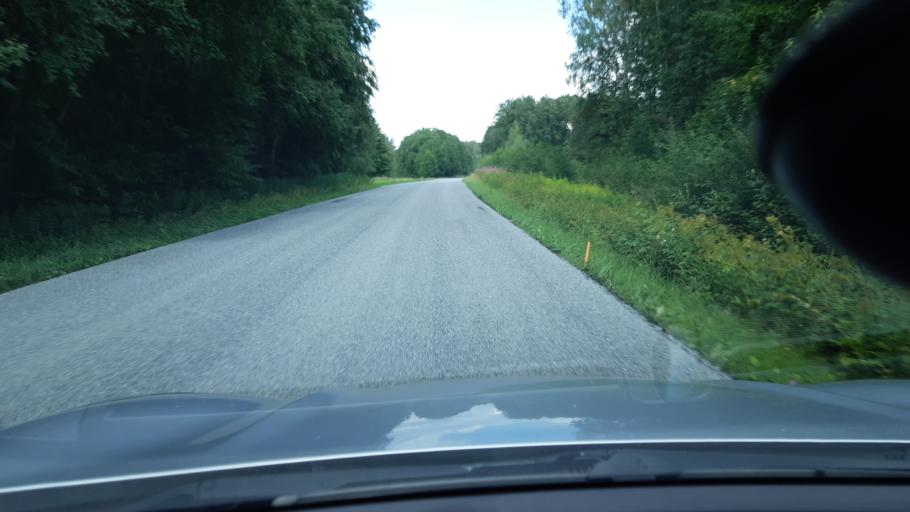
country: EE
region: Raplamaa
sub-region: Kehtna vald
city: Kehtna
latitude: 58.8967
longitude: 25.0268
